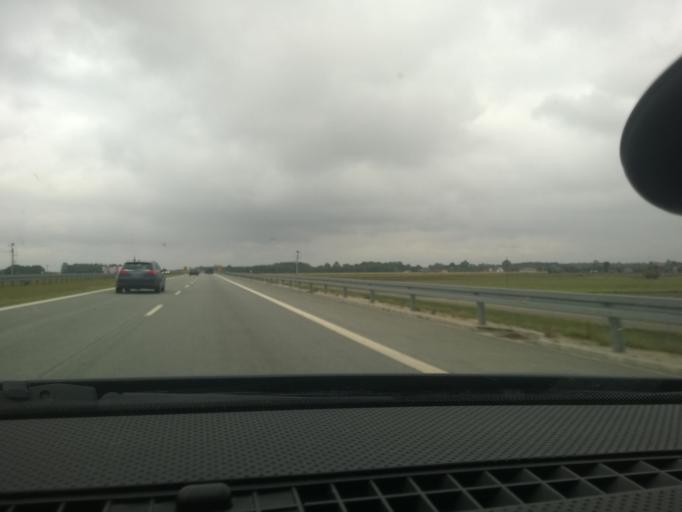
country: PL
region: Lodz Voivodeship
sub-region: Powiat laski
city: Sedziejowice
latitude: 51.5554
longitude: 19.0687
